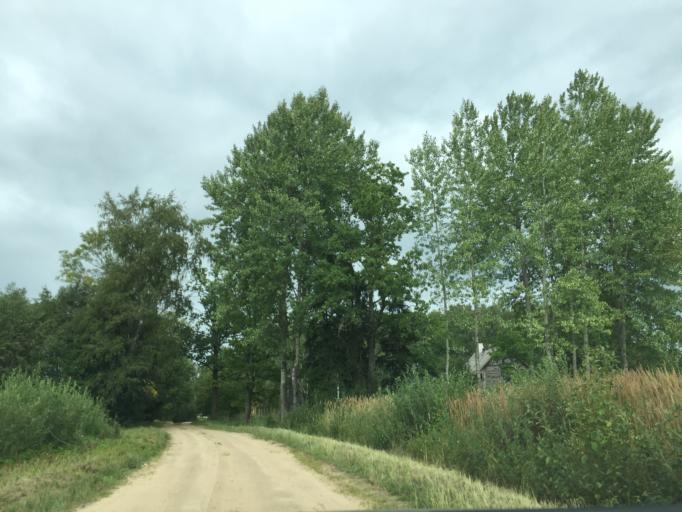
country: LV
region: Pargaujas
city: Stalbe
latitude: 57.5059
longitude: 24.9174
